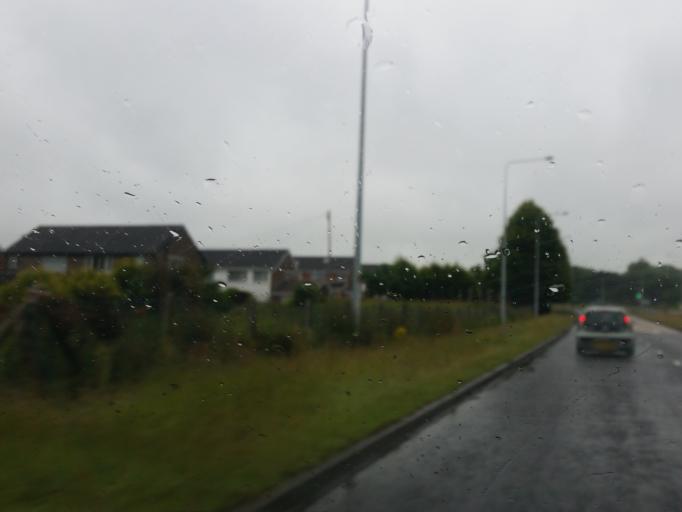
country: GB
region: Northern Ireland
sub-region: North Down District
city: Bangor
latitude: 54.6472
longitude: -5.6846
